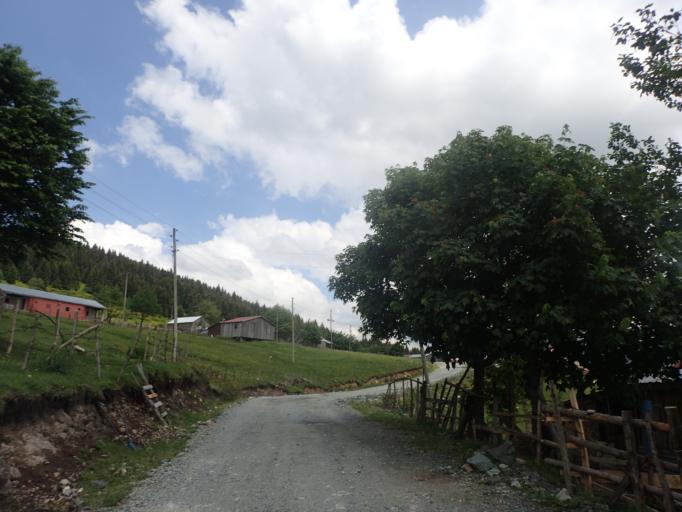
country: TR
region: Ordu
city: Topcam
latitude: 40.6841
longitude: 37.9459
